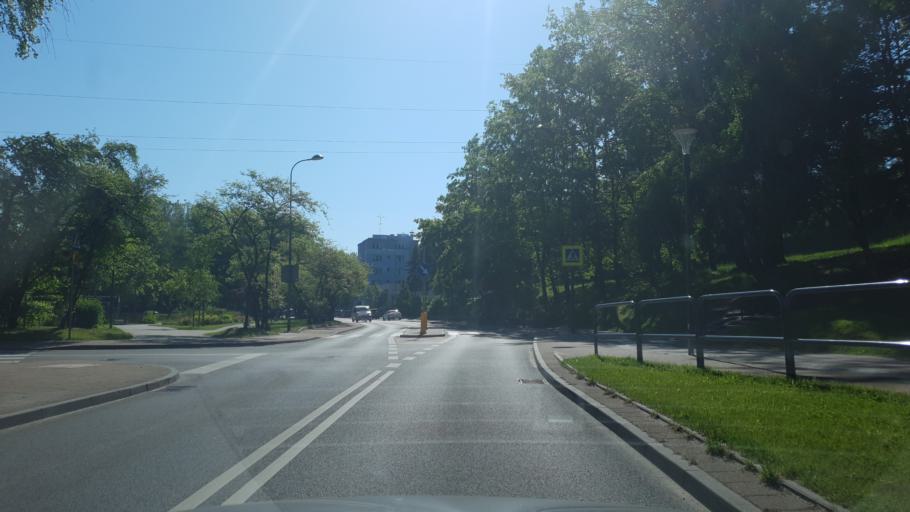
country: PL
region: Pomeranian Voivodeship
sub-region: Sopot
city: Sopot
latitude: 54.4557
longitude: 18.5504
